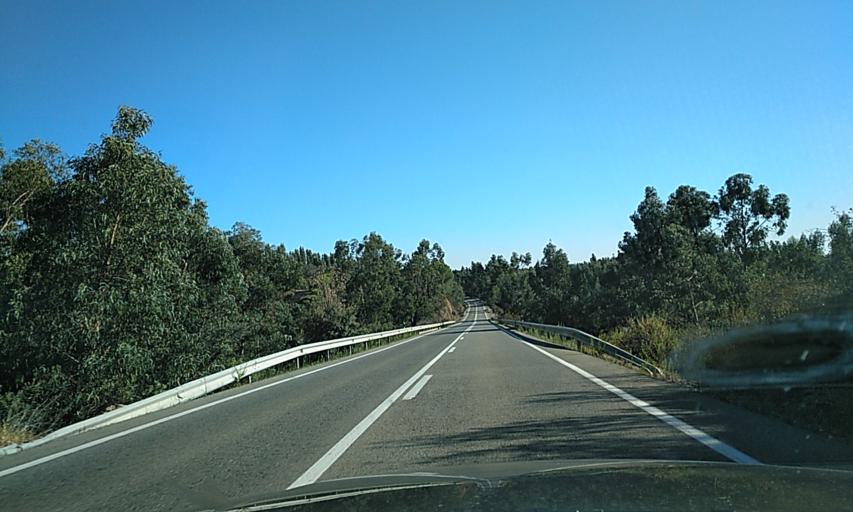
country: ES
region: Andalusia
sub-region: Provincia de Huelva
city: Santa Barbara de Casa
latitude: 37.8323
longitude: -7.2065
